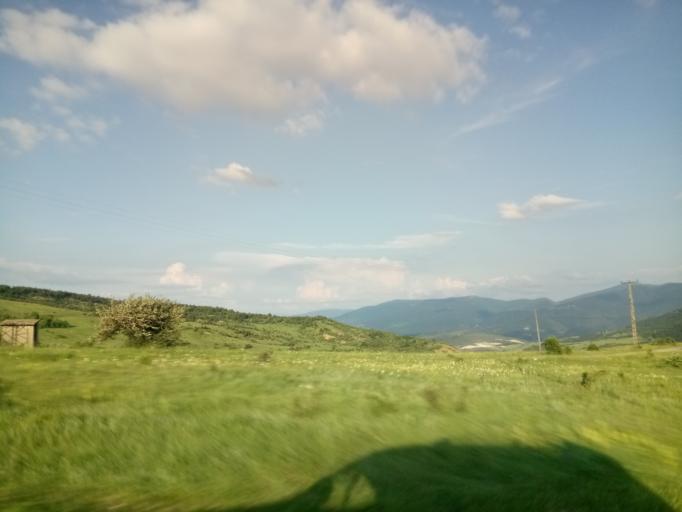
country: TR
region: Karabuk
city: Karabuk
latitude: 41.1001
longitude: 32.5948
